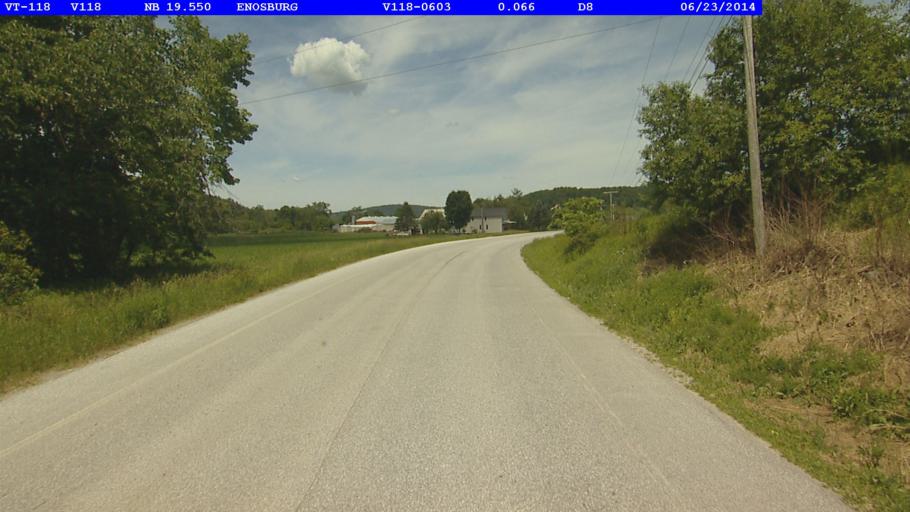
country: US
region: Vermont
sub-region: Franklin County
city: Richford
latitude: 44.9214
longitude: -72.6732
